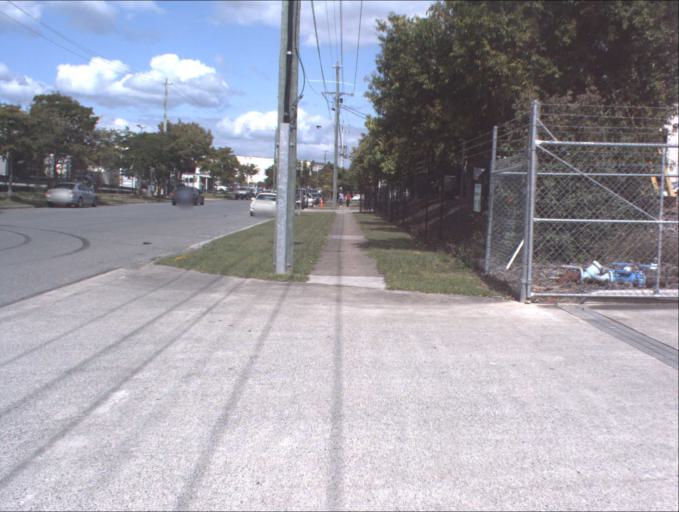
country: AU
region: Queensland
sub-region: Logan
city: Logan Reserve
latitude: -27.6814
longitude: 153.0760
